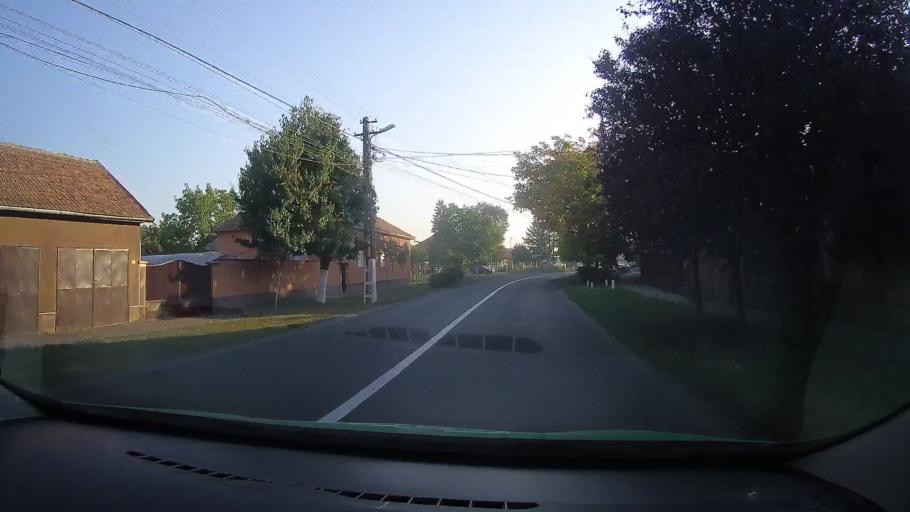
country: RO
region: Arad
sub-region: Comuna Curtici
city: Curtici
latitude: 46.3443
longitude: 21.3129
